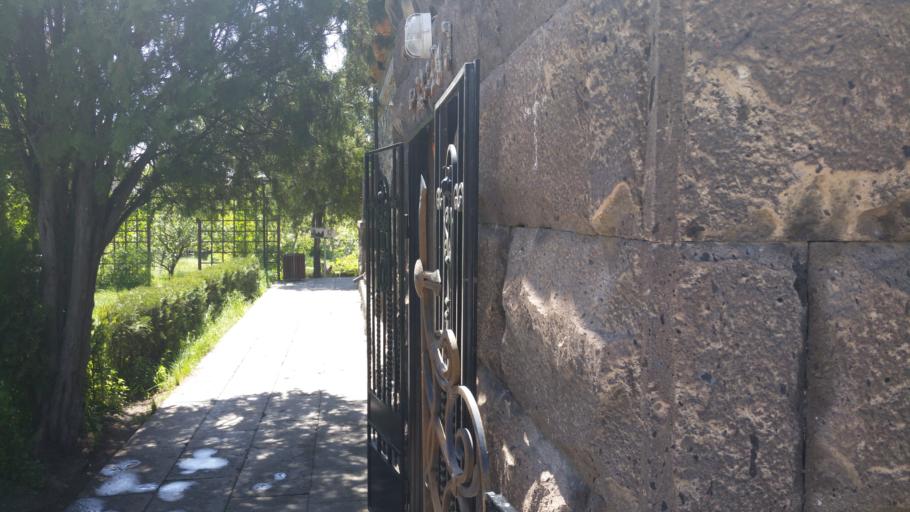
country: AM
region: Aragatsotn
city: Karbi
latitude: 40.3154
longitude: 44.3719
